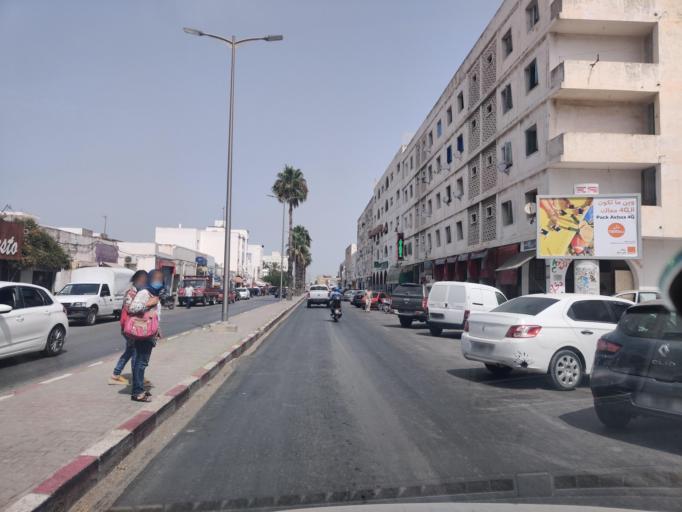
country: TN
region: Nabul
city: Bu `Urqub
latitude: 36.5991
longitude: 10.4986
